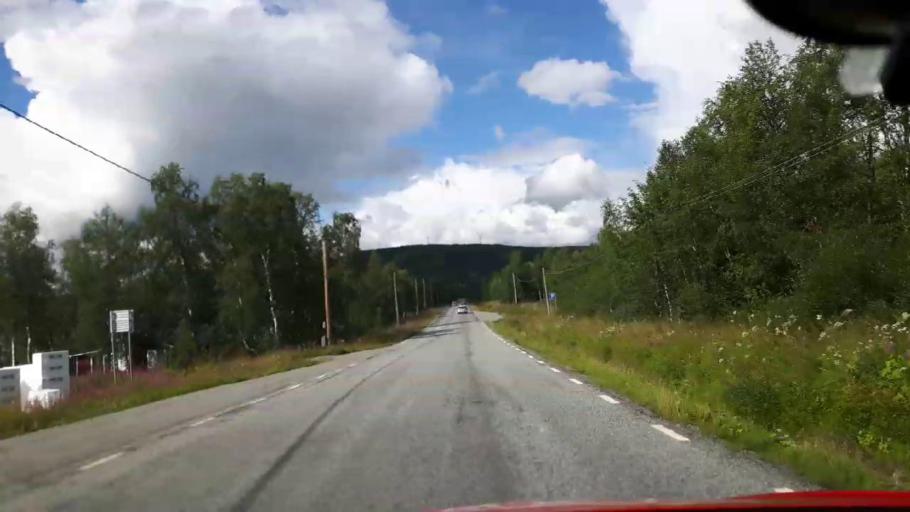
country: NO
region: Nordland
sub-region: Hattfjelldal
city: Hattfjelldal
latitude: 65.0643
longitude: 14.8437
